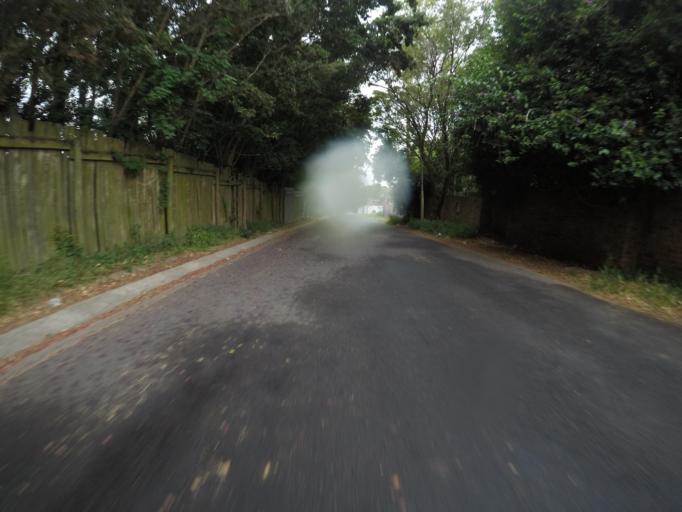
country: ZA
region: Eastern Cape
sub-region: Buffalo City Metropolitan Municipality
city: East London
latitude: -32.9887
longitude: 27.8579
